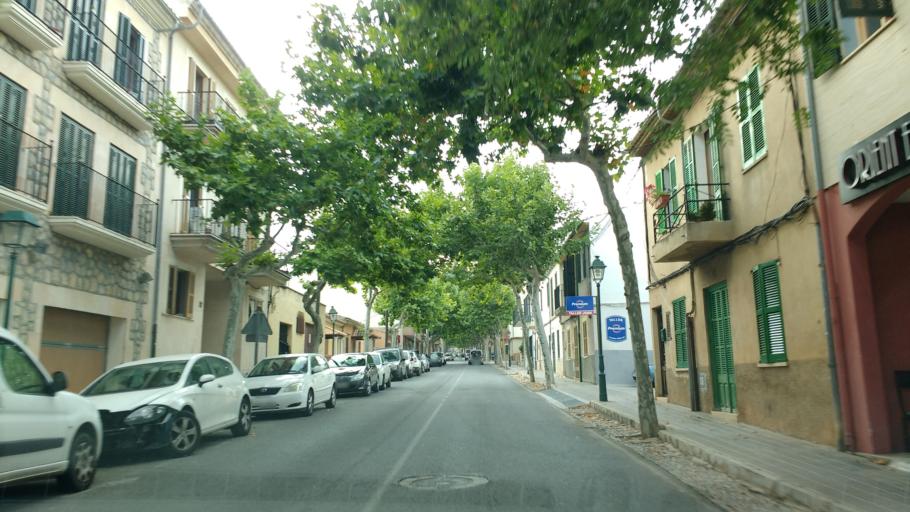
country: ES
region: Balearic Islands
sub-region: Illes Balears
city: Alaro
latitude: 39.7030
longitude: 2.7937
